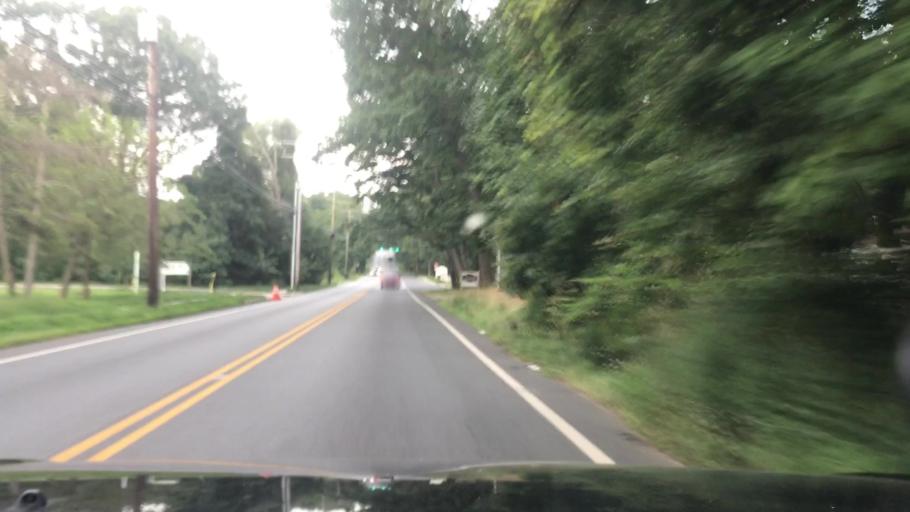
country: US
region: New Jersey
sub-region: Ocean County
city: Lakewood
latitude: 40.0758
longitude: -74.2503
